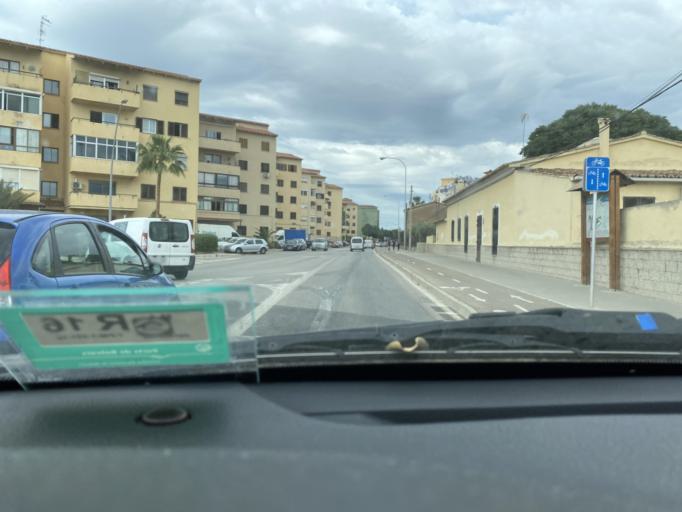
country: ES
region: Balearic Islands
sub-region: Illes Balears
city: Palma
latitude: 39.6037
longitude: 2.6759
